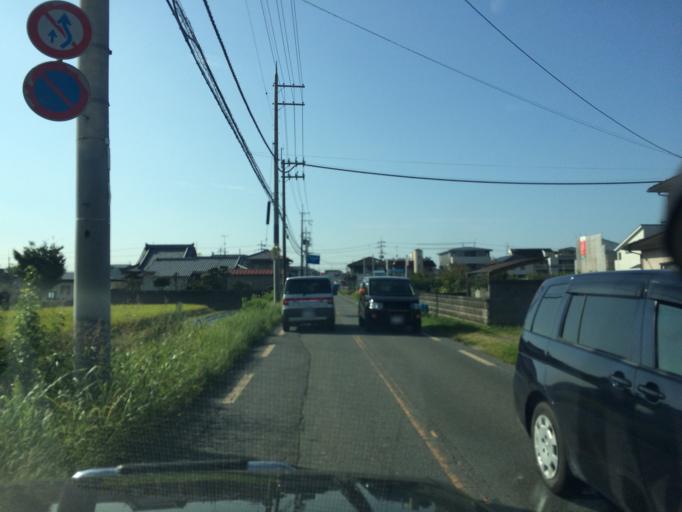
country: JP
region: Kyoto
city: Tanabe
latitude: 34.8012
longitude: 135.7888
